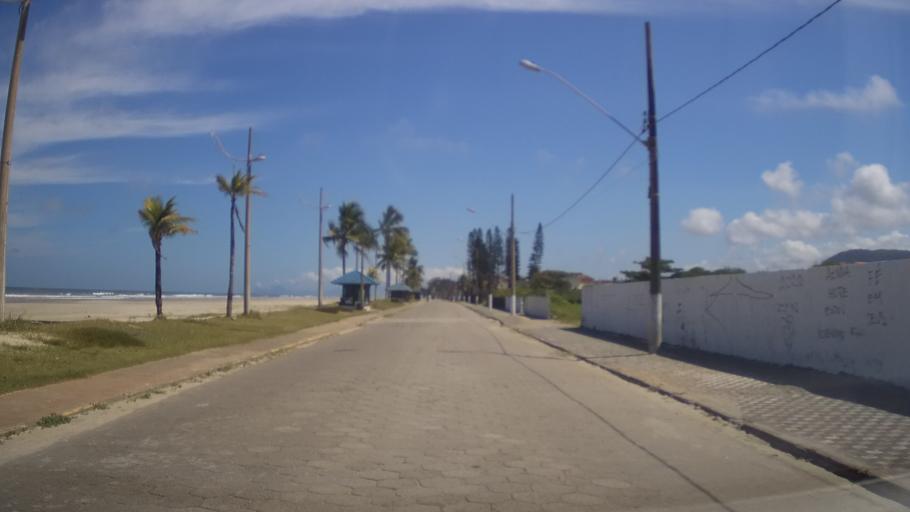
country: BR
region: Sao Paulo
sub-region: Mongagua
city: Mongagua
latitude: -24.1352
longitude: -46.6961
